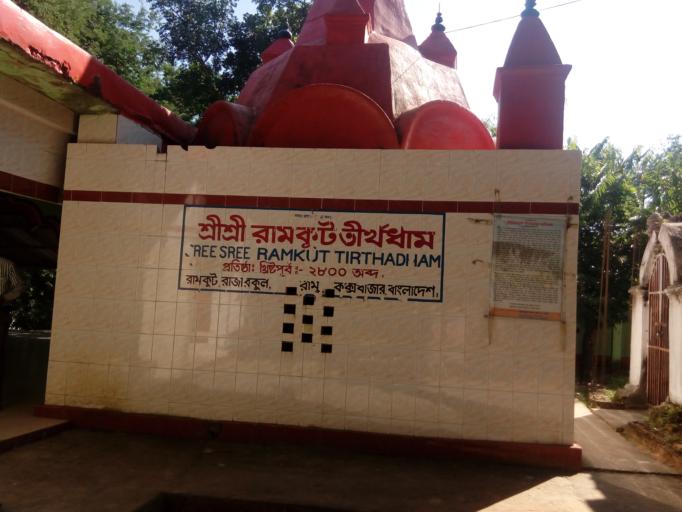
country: BD
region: Chittagong
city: Cox's Bazar
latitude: 21.4011
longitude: 92.1121
